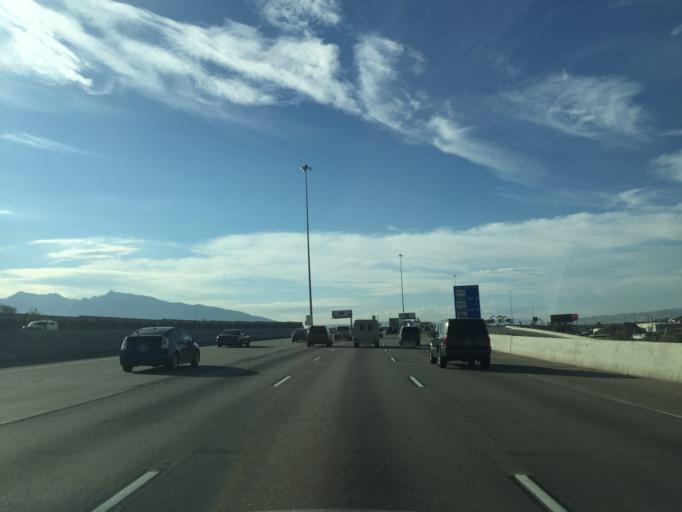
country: US
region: Utah
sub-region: Salt Lake County
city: Centerfield
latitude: 40.6993
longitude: -111.9022
